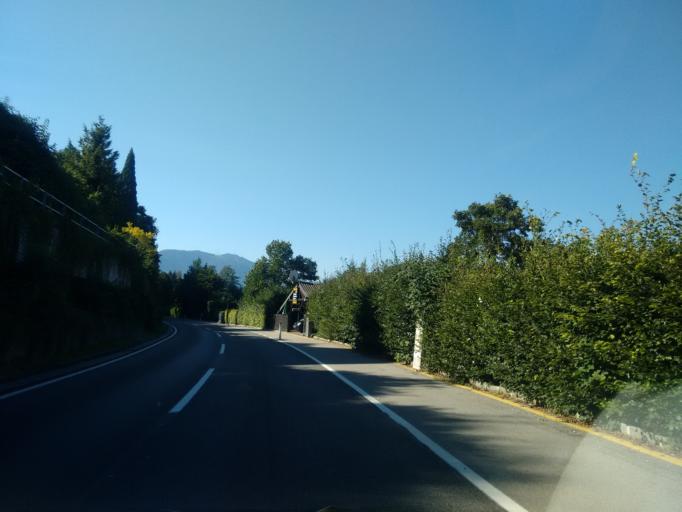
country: AT
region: Upper Austria
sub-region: Politischer Bezirk Vocklabruck
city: Steinbach am Attersee
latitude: 47.8442
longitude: 13.5479
